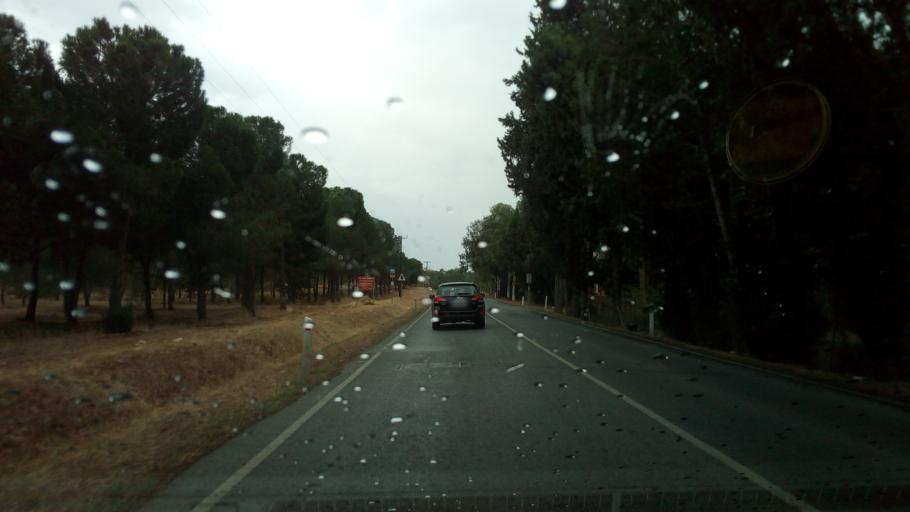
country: CY
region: Lefkosia
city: Nicosia
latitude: 35.1378
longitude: 33.3781
